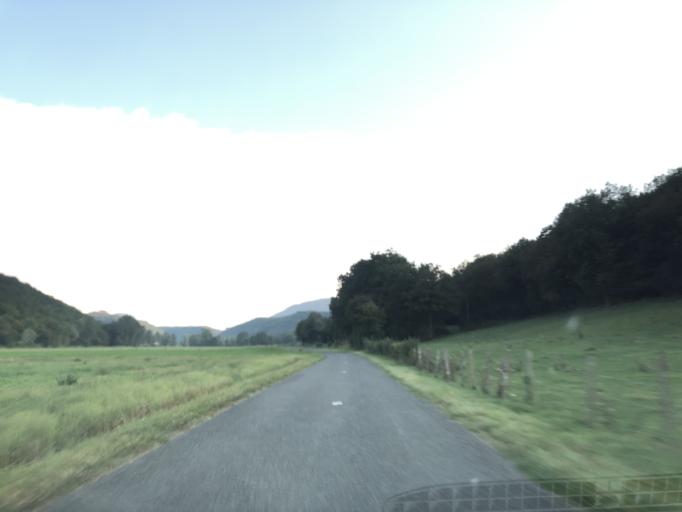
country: FR
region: Rhone-Alpes
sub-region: Departement de l'Ain
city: Belley
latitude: 45.7482
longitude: 5.6219
